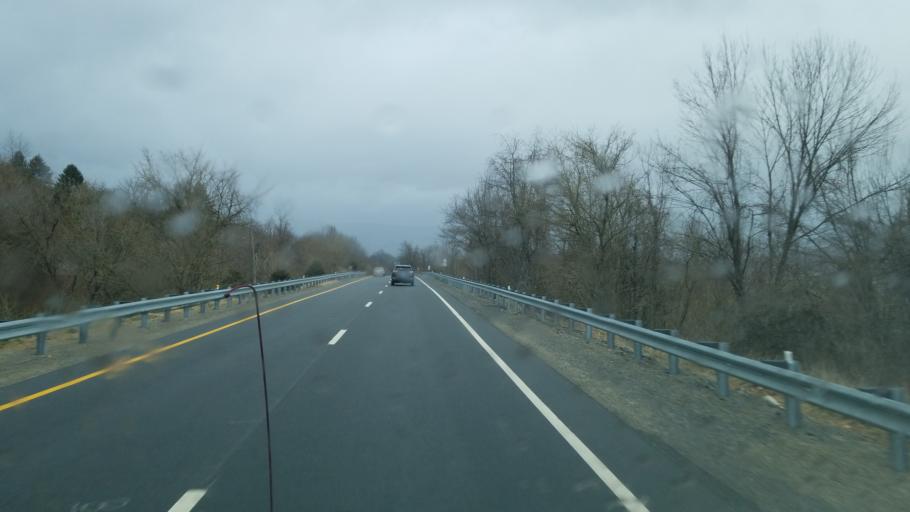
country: US
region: Virginia
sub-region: Giles County
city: Pearisburg
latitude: 37.2981
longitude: -80.7397
